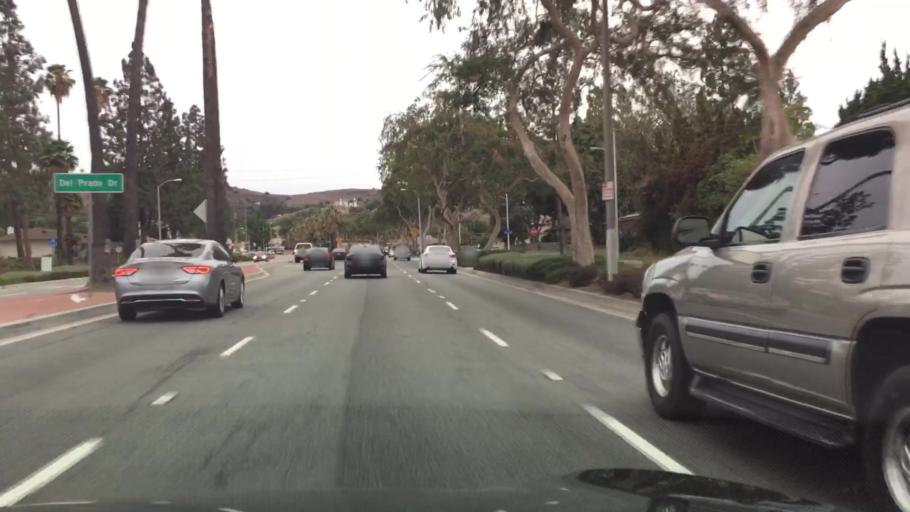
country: US
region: California
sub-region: Los Angeles County
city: Hacienda Heights
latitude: 33.9848
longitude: -117.9719
